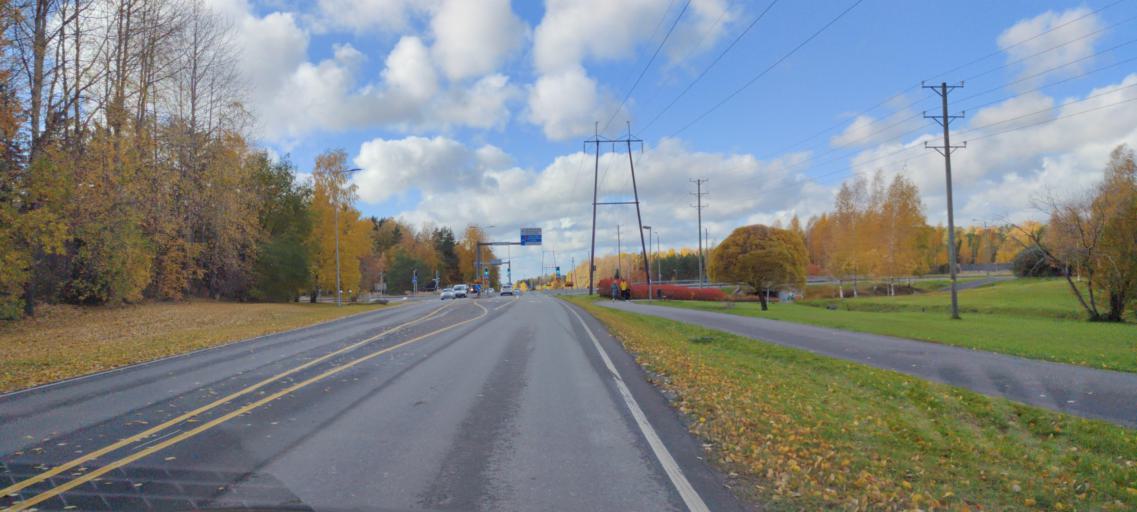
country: FI
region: Varsinais-Suomi
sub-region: Turku
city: Kaarina
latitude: 60.4064
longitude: 22.3454
